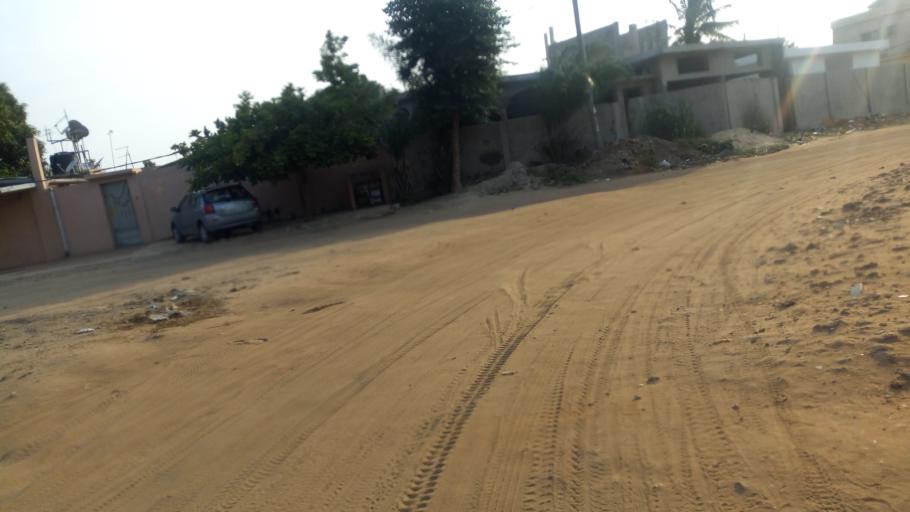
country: TG
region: Maritime
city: Lome
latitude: 6.1923
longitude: 1.1790
